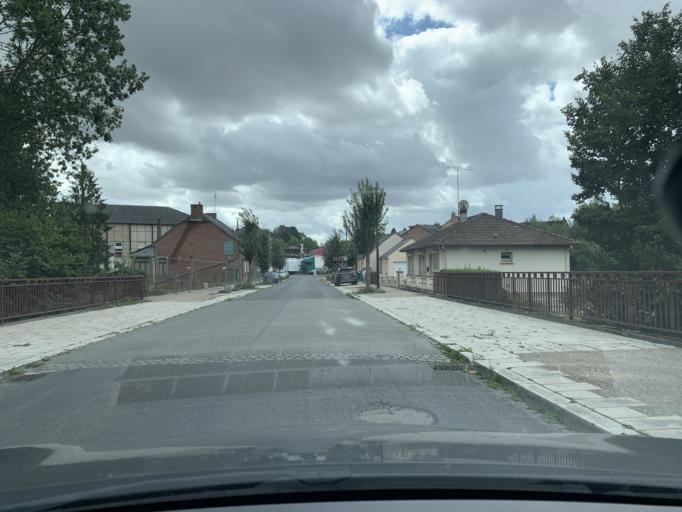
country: FR
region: Picardie
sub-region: Departement de l'Aisne
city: Saint-Michel
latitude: 49.9205
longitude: 4.1347
